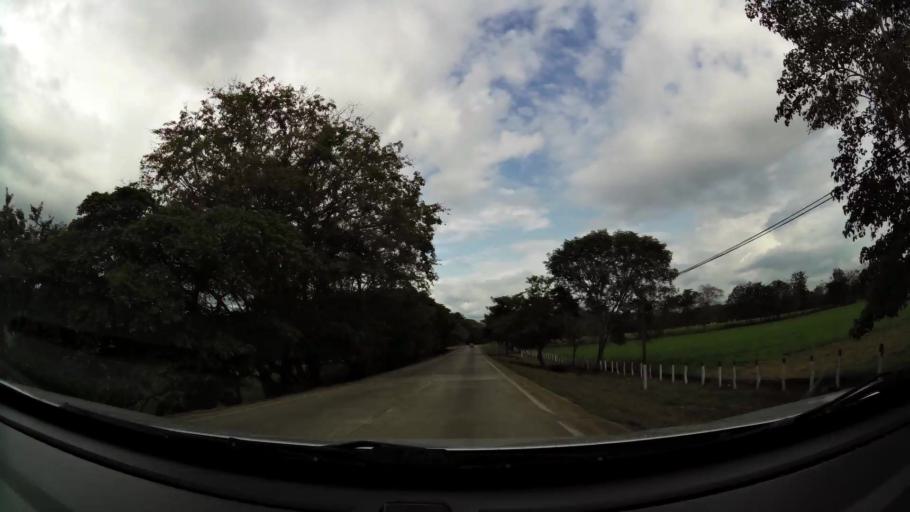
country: CR
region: Guanacaste
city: Juntas
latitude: 10.2638
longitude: -85.0313
